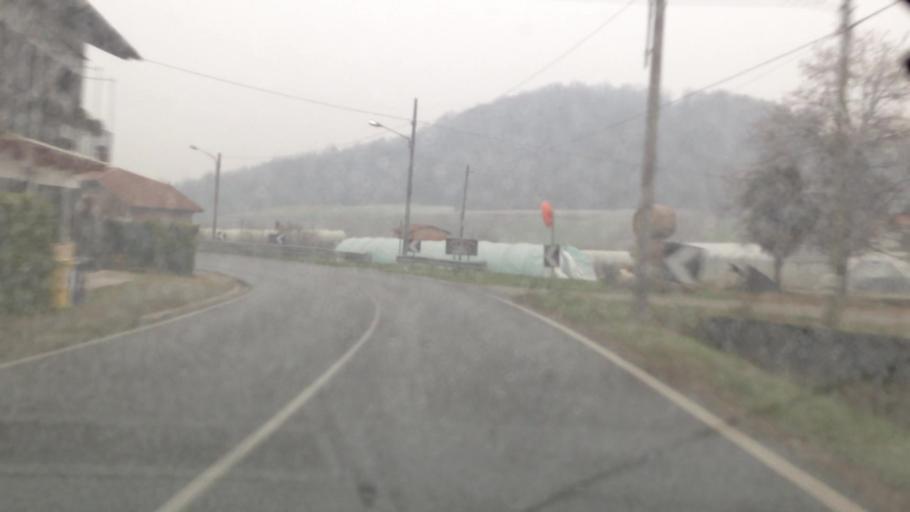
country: IT
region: Piedmont
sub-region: Provincia di Torino
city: Brozolo
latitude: 45.1032
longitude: 8.0740
